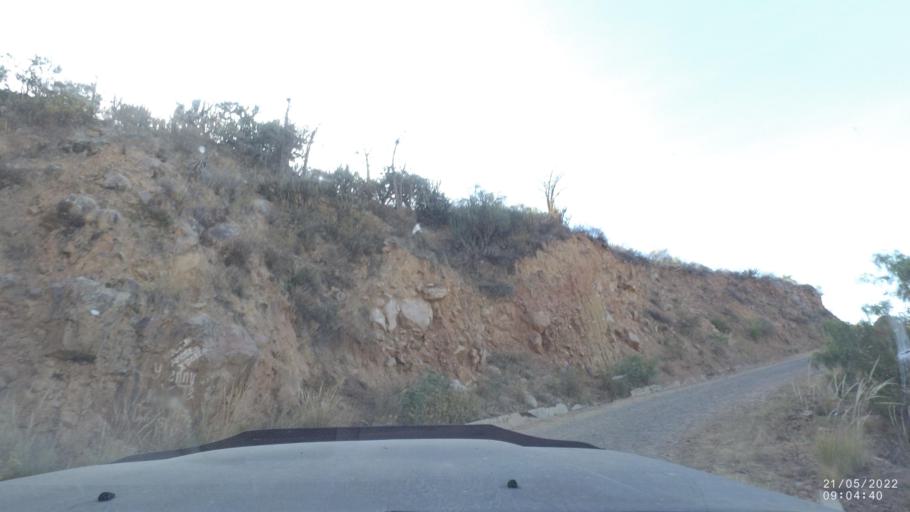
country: BO
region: Cochabamba
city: Cochabamba
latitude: -17.3788
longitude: -66.0256
